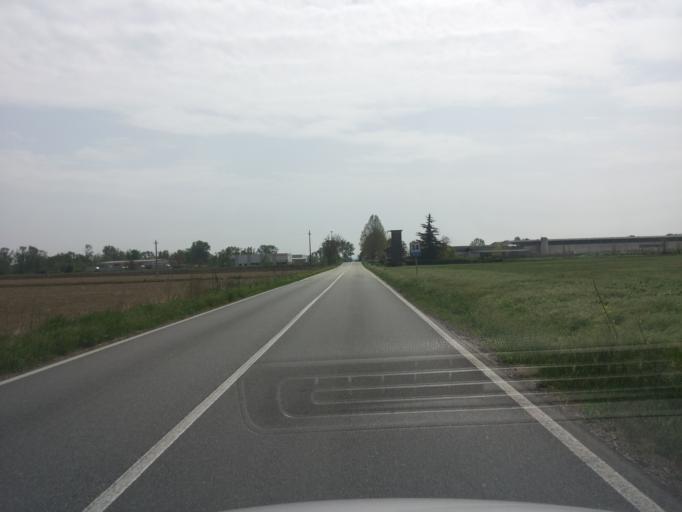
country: IT
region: Piedmont
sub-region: Provincia di Alessandria
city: Occimiano
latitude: 45.0771
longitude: 8.4827
